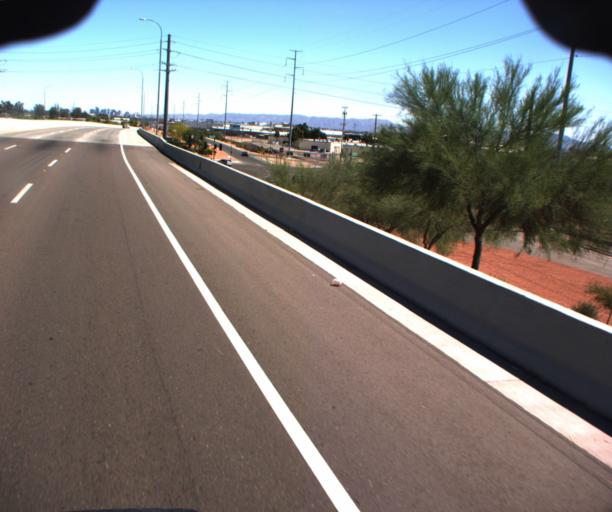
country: US
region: Arizona
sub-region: Maricopa County
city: Glendale
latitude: 33.5106
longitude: -112.1523
